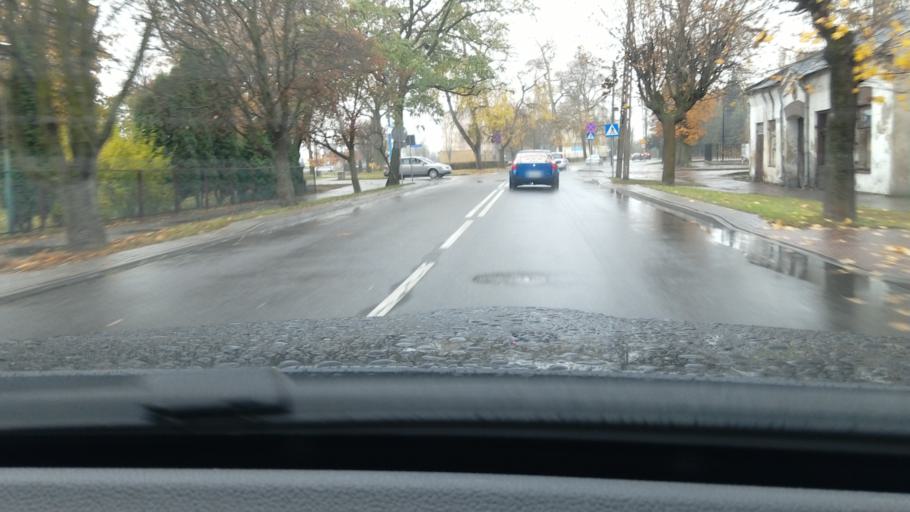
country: PL
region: Lodz Voivodeship
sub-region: Skierniewice
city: Skierniewice
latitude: 51.9496
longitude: 20.1434
